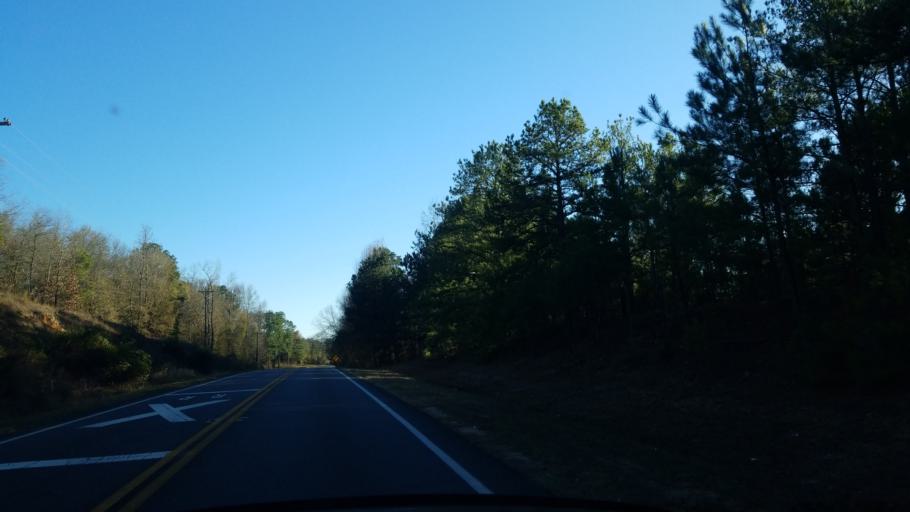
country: US
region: Georgia
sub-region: Talbot County
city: Talbotton
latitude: 32.5473
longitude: -84.6022
